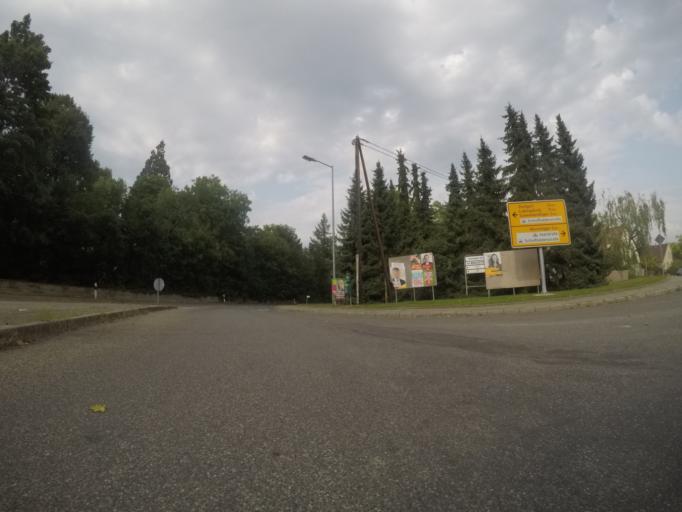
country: DE
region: Baden-Wuerttemberg
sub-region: Regierungsbezirk Stuttgart
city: Hemmingen
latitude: 48.8657
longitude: 9.0369
